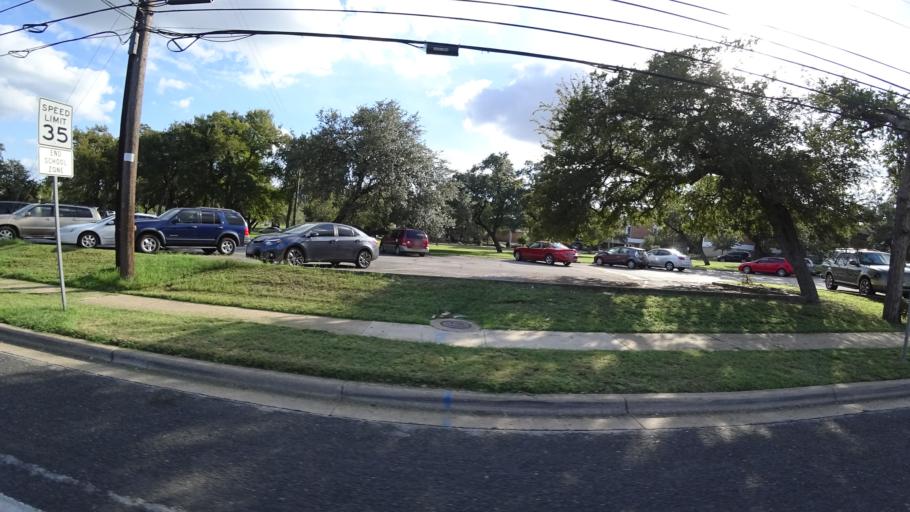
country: US
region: Texas
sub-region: Travis County
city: Rollingwood
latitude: 30.2144
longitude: -97.7957
